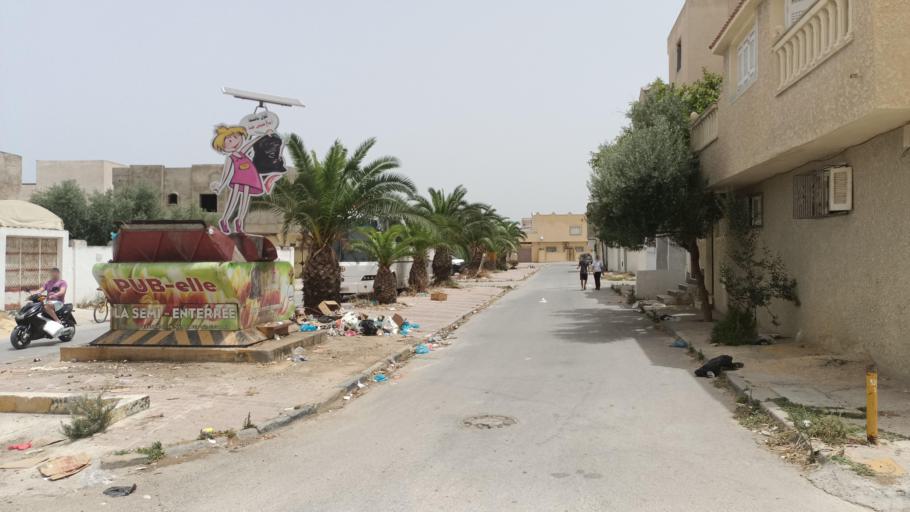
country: TN
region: Nabul
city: Manzil Bu Zalafah
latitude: 36.7016
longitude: 10.4902
